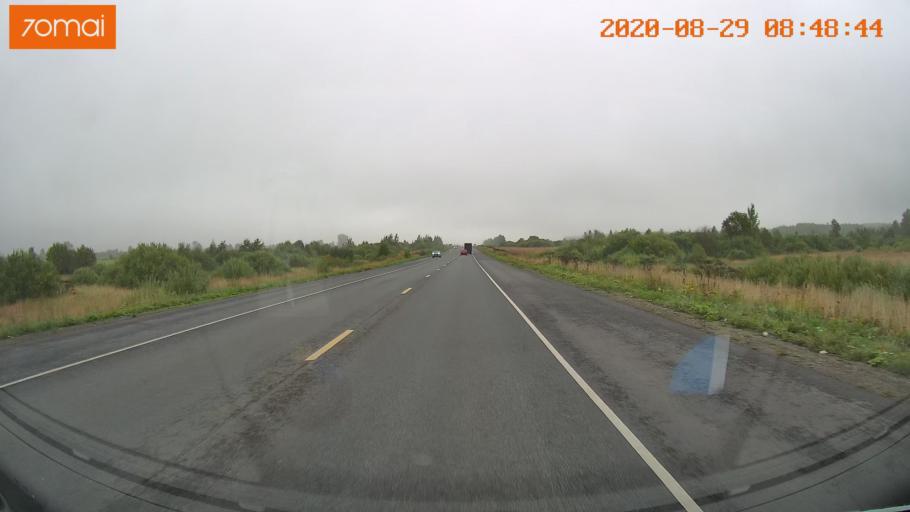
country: RU
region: Ivanovo
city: Vichuga
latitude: 57.1644
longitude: 41.8547
